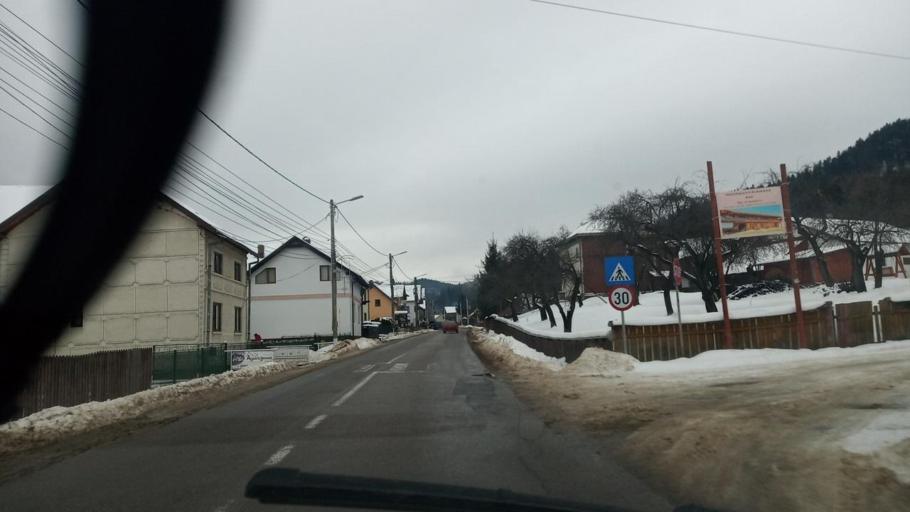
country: RO
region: Suceava
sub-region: Oras Gura Humorului
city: Gura Humorului
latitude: 47.5349
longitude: 25.8648
